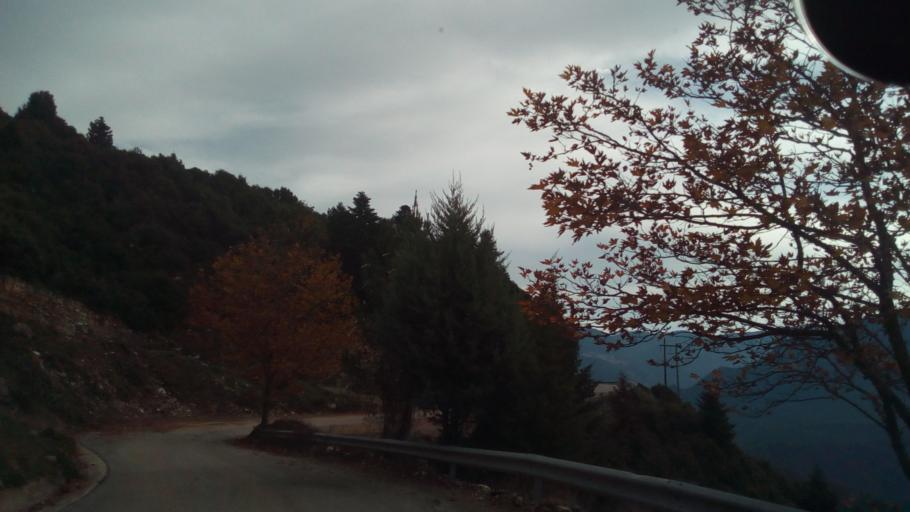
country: GR
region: West Greece
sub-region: Nomos Aitolias kai Akarnanias
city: Thermo
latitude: 38.6818
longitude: 21.8727
